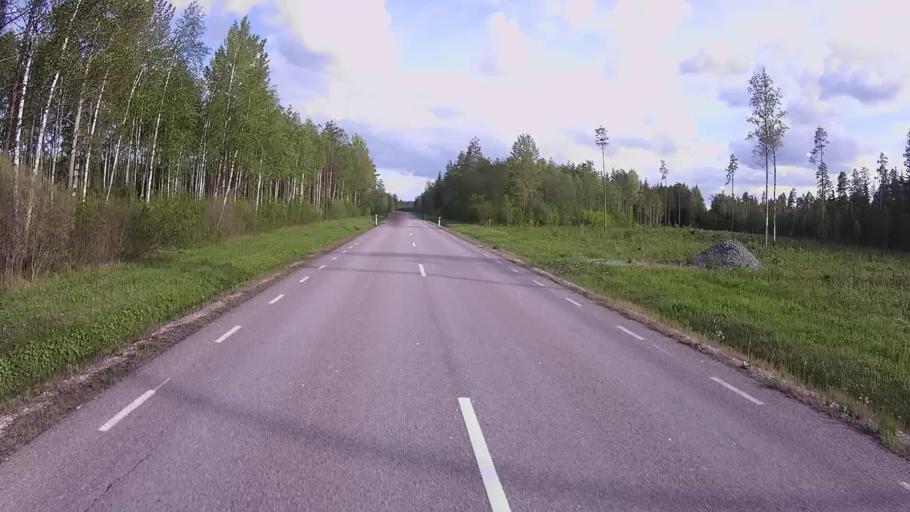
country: EE
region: Jogevamaa
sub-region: Mustvee linn
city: Mustvee
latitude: 59.0701
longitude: 26.9988
